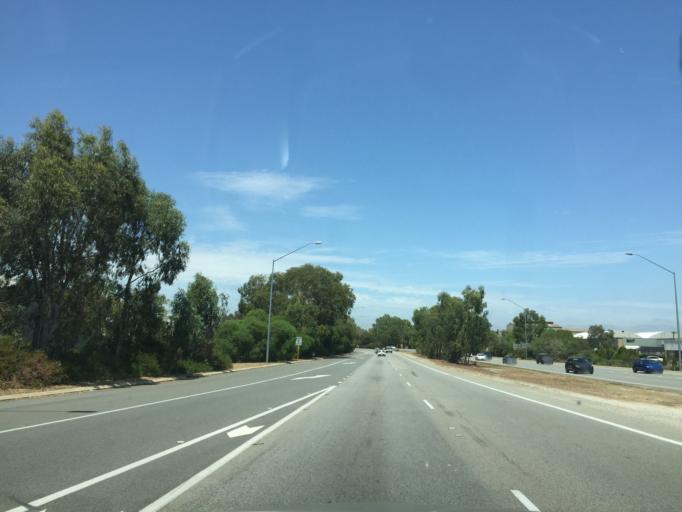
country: AU
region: Western Australia
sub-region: Canning
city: Bentley
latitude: -31.9879
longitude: 115.9320
